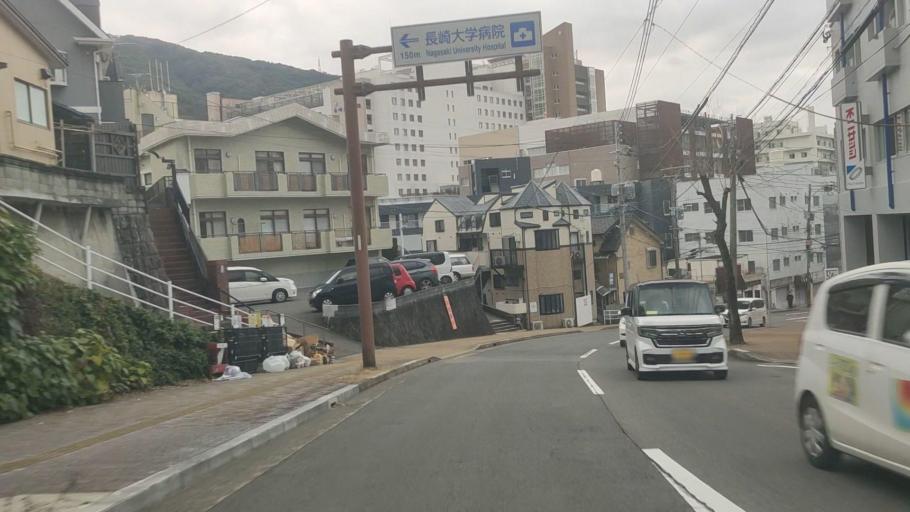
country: JP
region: Nagasaki
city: Nagasaki-shi
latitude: 32.7715
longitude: 129.8673
